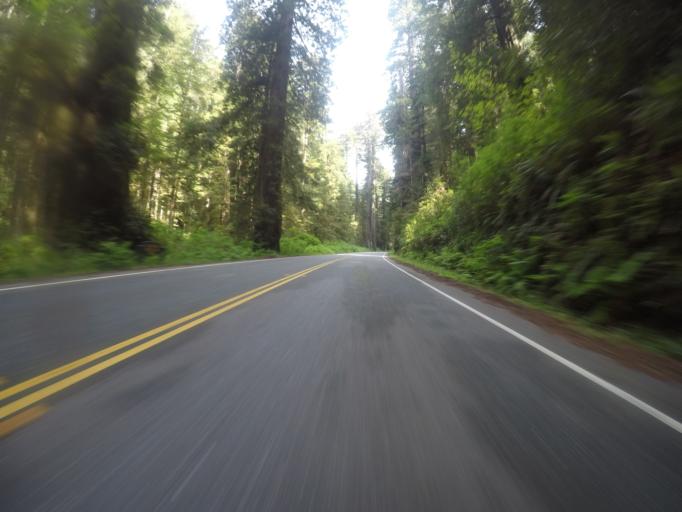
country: US
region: California
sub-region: Del Norte County
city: Bertsch-Oceanview
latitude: 41.4356
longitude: -124.0397
